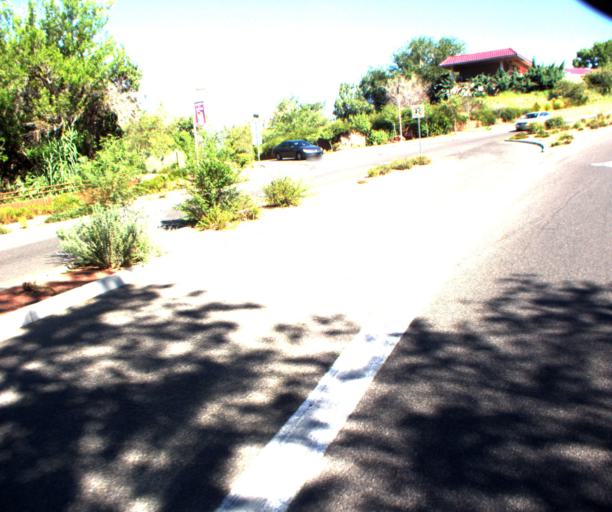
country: US
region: Arizona
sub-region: Coconino County
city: Sedona
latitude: 34.8633
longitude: -111.7637
